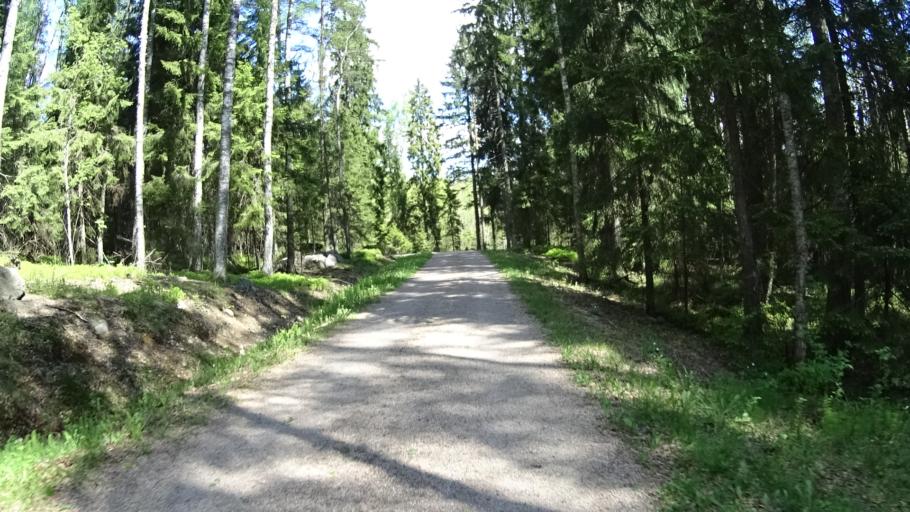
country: FI
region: Uusimaa
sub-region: Helsinki
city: Espoo
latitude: 60.2083
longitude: 24.6217
